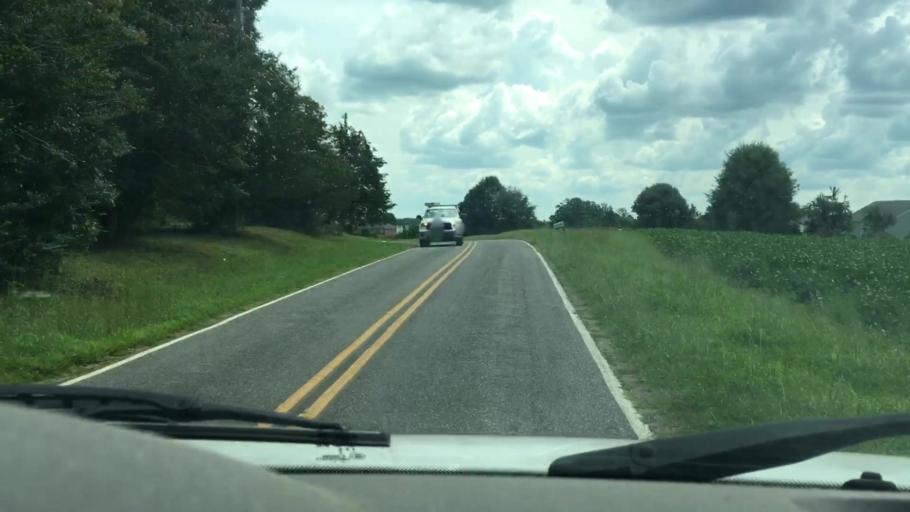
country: US
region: North Carolina
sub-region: Iredell County
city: Troutman
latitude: 35.6679
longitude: -80.8319
